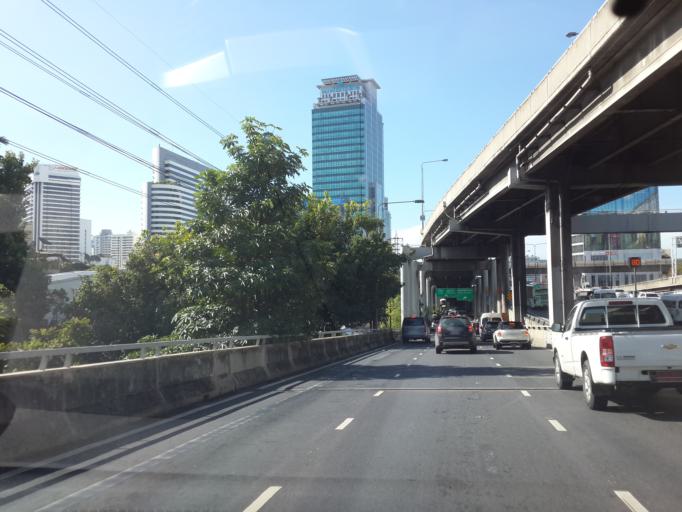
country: TH
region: Bangkok
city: Ratchathewi
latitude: 13.7448
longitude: 100.5504
